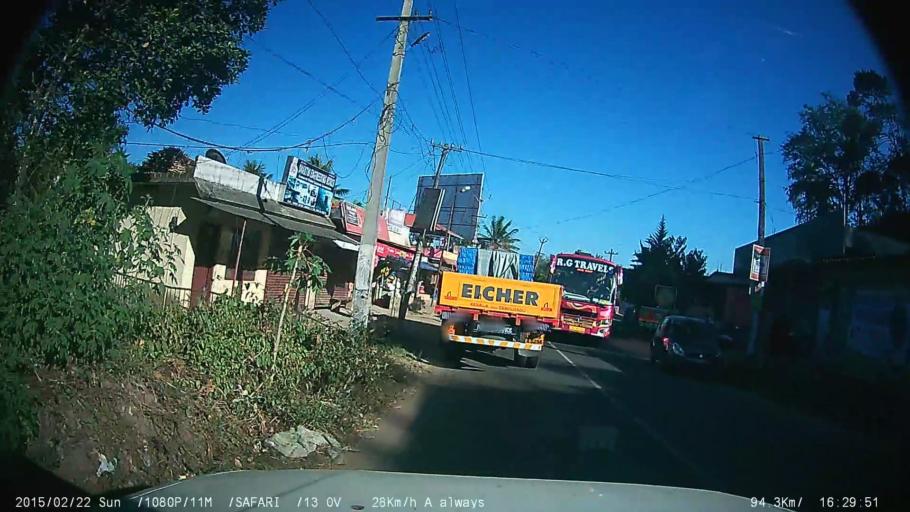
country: IN
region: Tamil Nadu
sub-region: Theni
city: Gudalur
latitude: 9.6140
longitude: 77.1561
